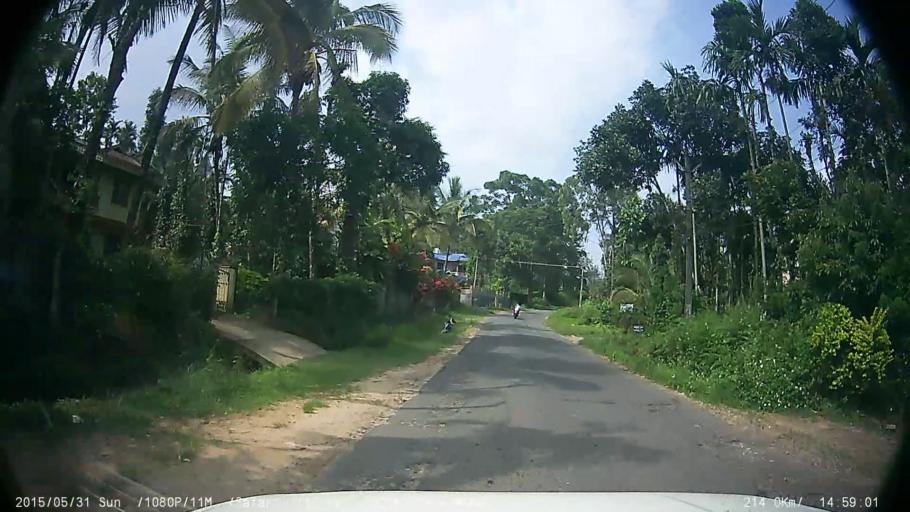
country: IN
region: Kerala
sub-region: Wayanad
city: Kalpetta
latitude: 11.6082
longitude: 76.2080
